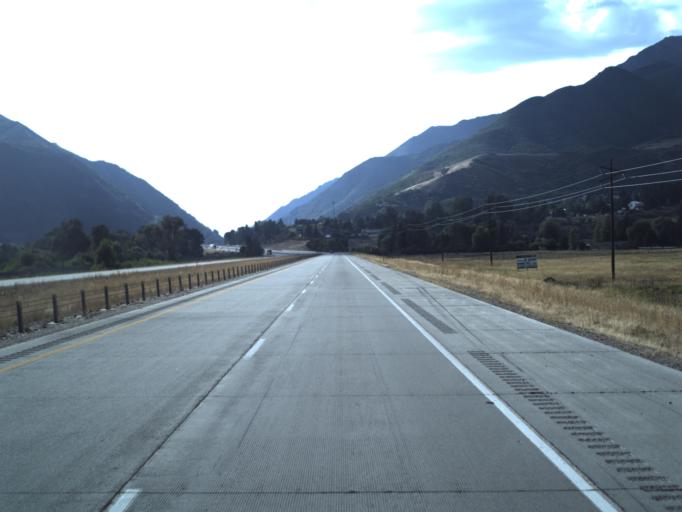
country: US
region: Utah
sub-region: Morgan County
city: Mountain Green
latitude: 41.1390
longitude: -111.8129
